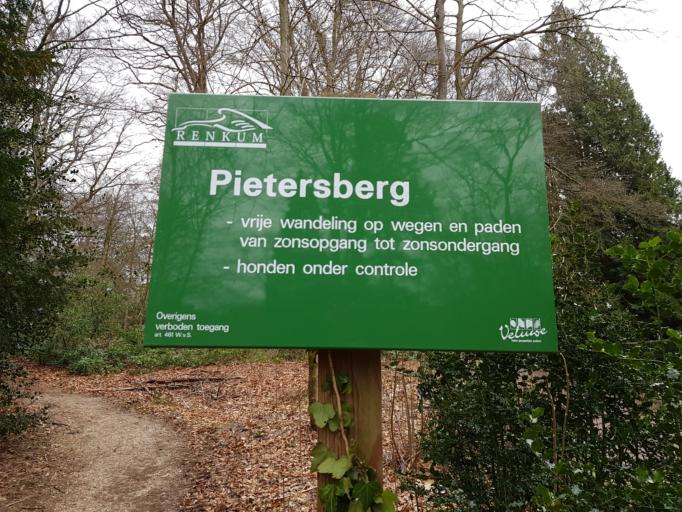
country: NL
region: Gelderland
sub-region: Gemeente Renkum
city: Oosterbeek
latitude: 51.9819
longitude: 5.8331
